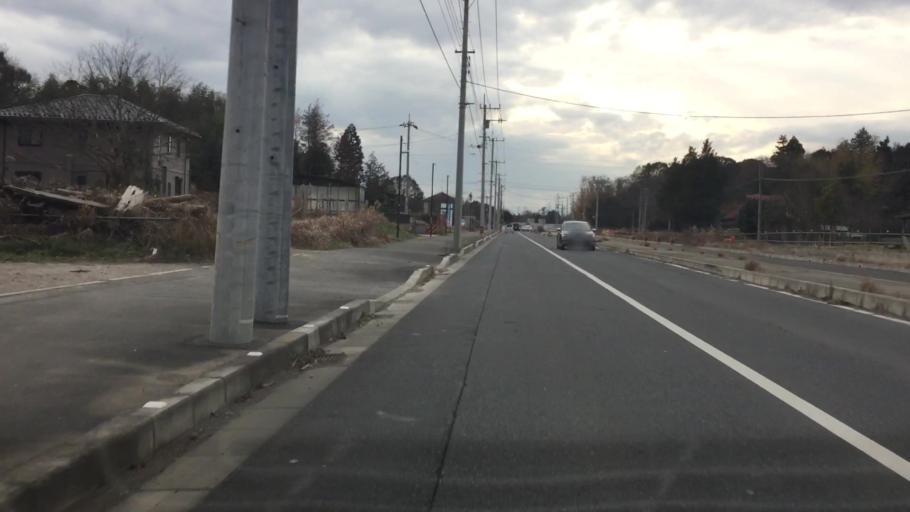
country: JP
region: Chiba
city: Shiroi
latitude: 35.7974
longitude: 140.0925
